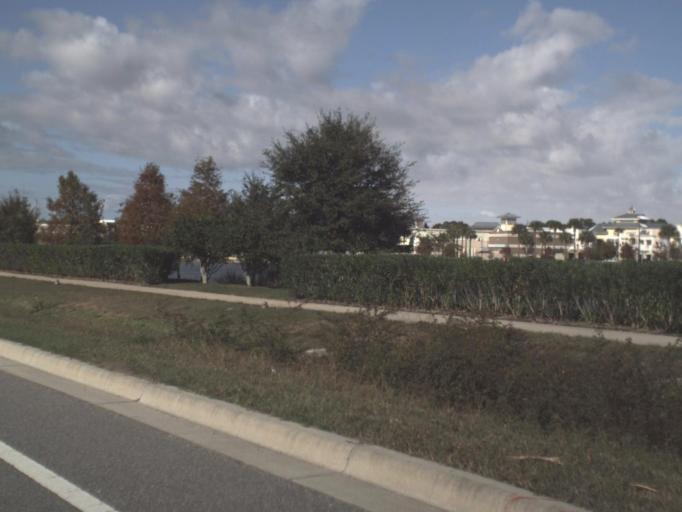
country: US
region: Florida
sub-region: Volusia County
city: Port Orange
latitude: 29.1067
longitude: -81.0327
